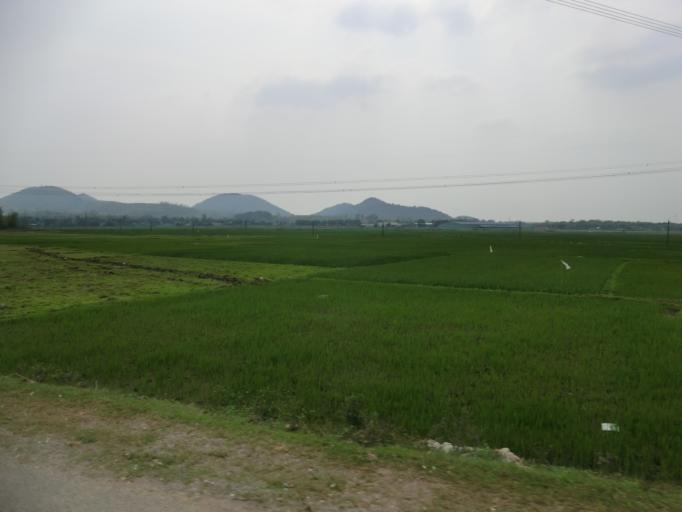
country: VN
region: Nghe An
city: Cau Giat
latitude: 19.3070
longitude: 105.4748
